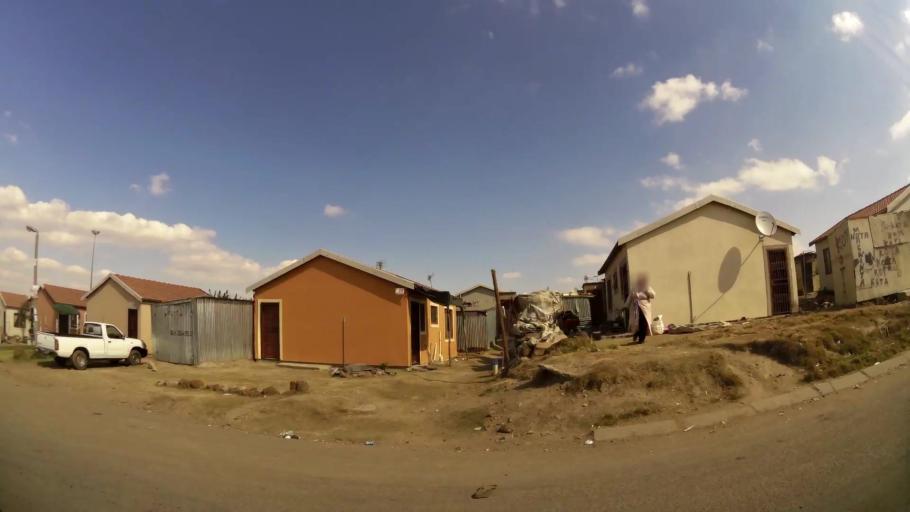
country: ZA
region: Gauteng
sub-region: Ekurhuleni Metropolitan Municipality
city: Tembisa
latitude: -26.0299
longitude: 28.1879
